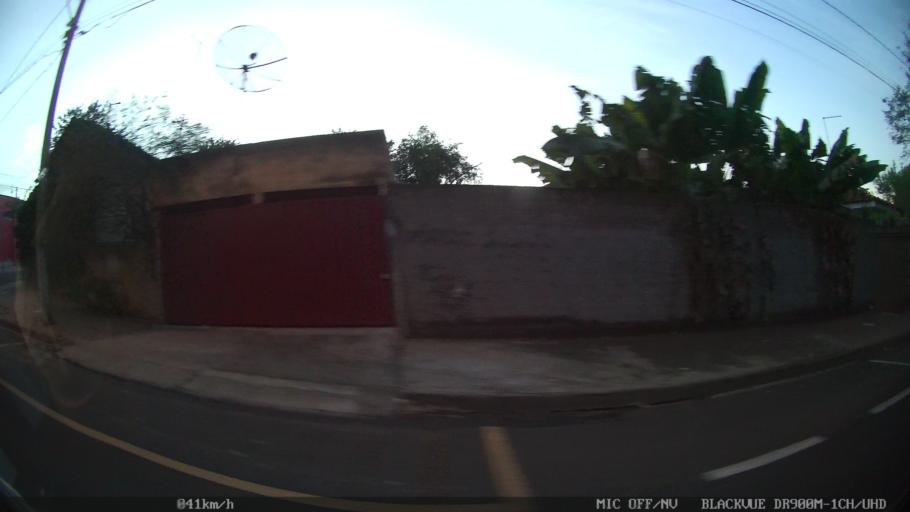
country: BR
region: Sao Paulo
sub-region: Catanduva
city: Catanduva
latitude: -21.1493
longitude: -48.9937
